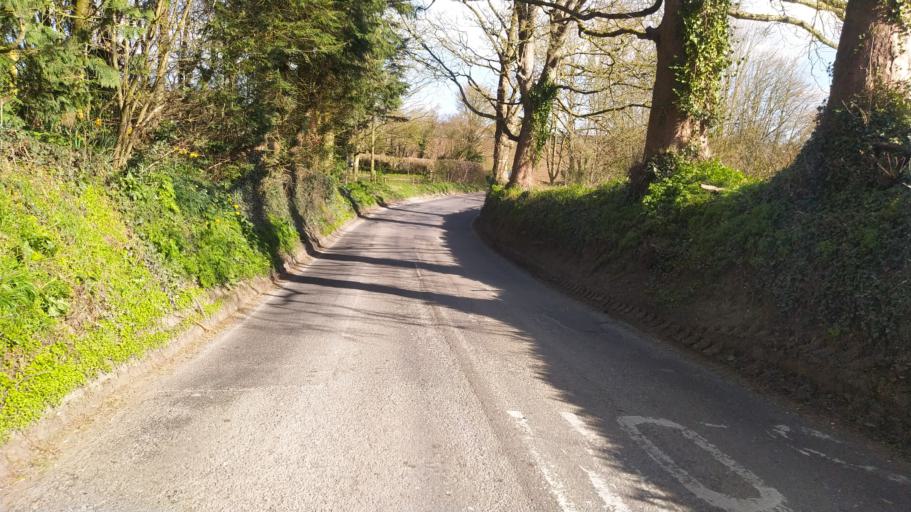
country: GB
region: England
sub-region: Dorset
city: Sturminster Newton
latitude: 50.9632
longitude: -2.3144
